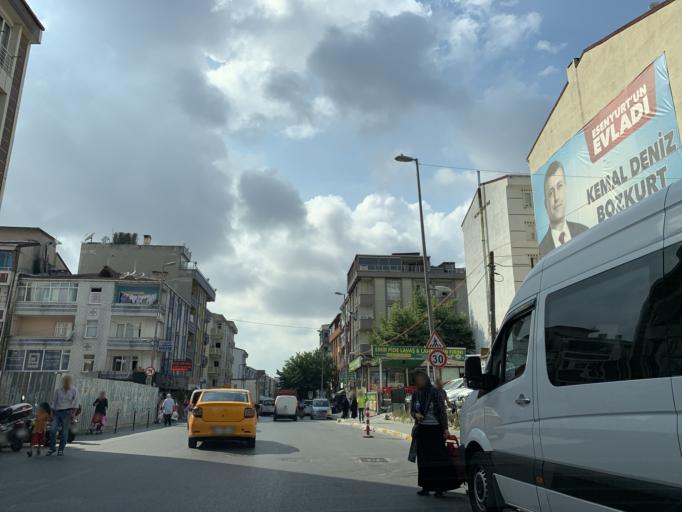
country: TR
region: Istanbul
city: Esenyurt
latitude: 41.0216
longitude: 28.6739
